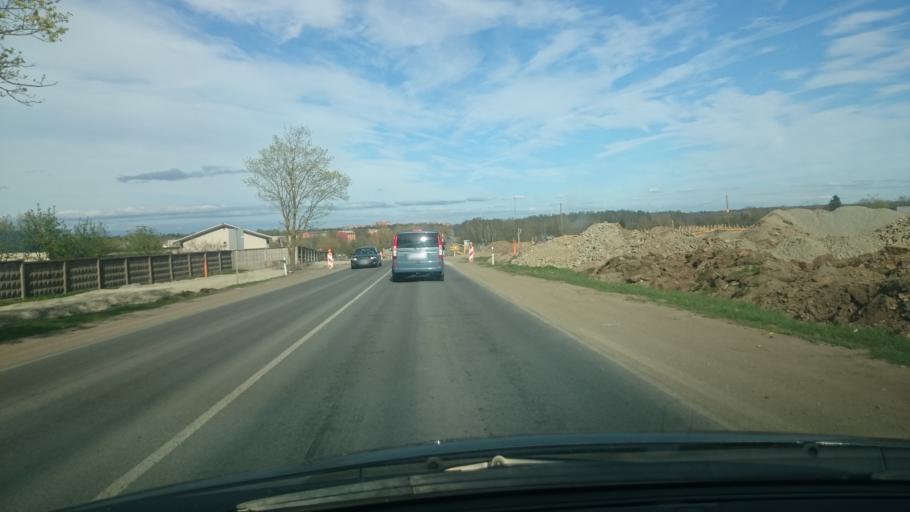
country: EE
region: Ida-Virumaa
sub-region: Sillamaee linn
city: Sillamae
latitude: 59.3913
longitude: 27.7462
